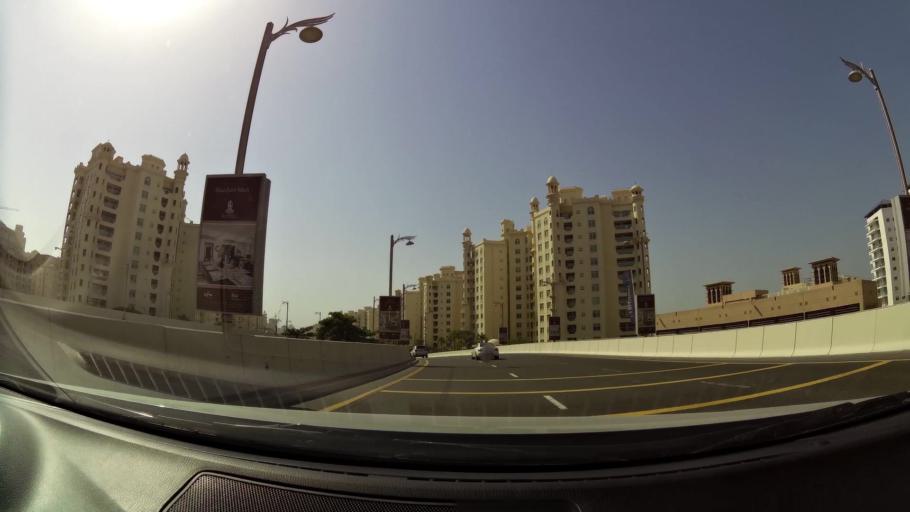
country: AE
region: Dubai
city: Dubai
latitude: 25.1058
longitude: 55.1513
